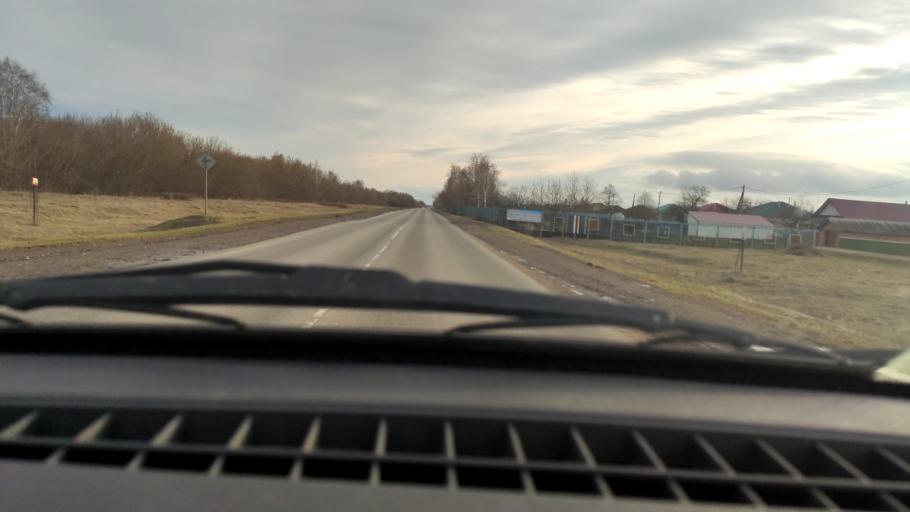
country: RU
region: Bashkortostan
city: Davlekanovo
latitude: 54.3006
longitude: 55.1321
